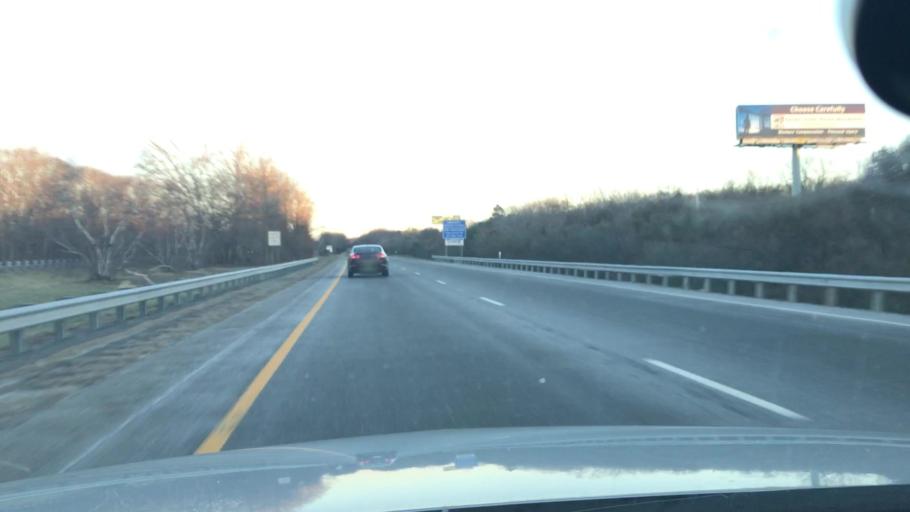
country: US
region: New Jersey
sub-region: Camden County
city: Sicklerville
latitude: 39.7294
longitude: -75.0050
